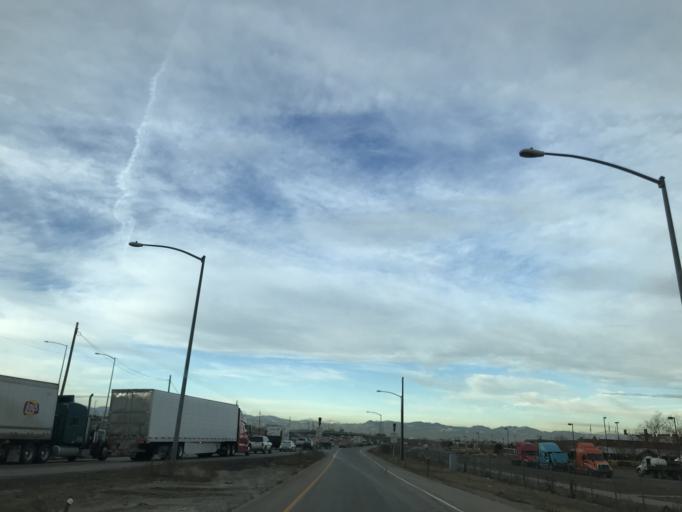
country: US
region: Colorado
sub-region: Adams County
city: Commerce City
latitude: 39.7787
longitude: -104.8877
